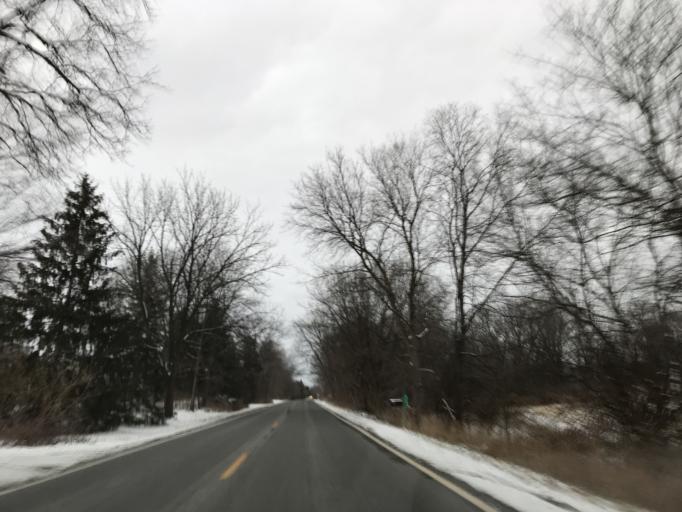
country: US
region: Michigan
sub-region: Washtenaw County
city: Ann Arbor
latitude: 42.3383
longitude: -83.7184
